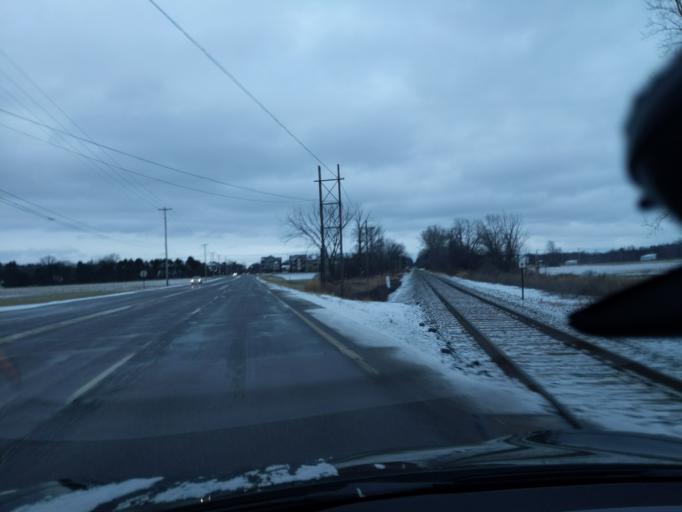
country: US
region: Michigan
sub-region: Ingham County
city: East Lansing
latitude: 42.7118
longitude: -84.4673
